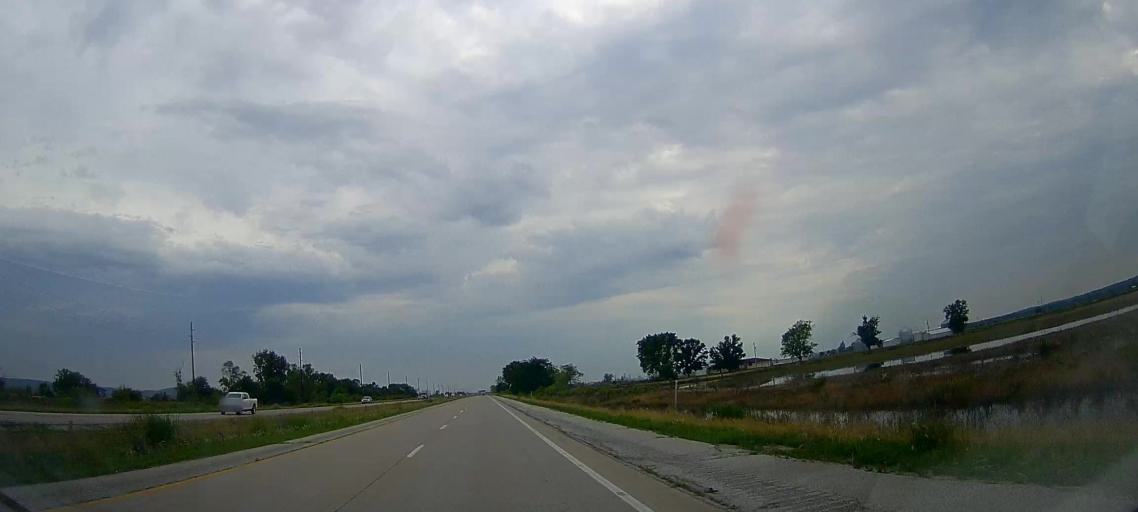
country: US
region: Iowa
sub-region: Pottawattamie County
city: Carter Lake
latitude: 41.3964
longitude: -95.8997
